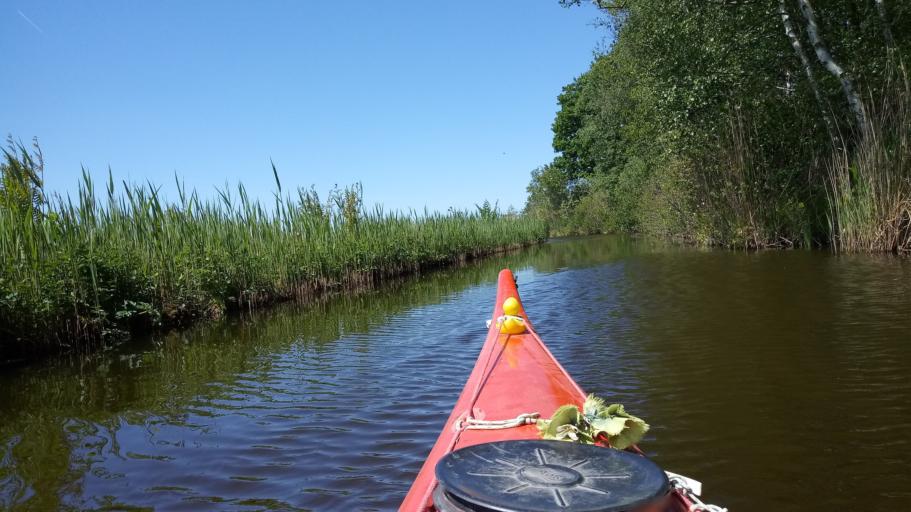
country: NL
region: South Holland
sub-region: Gemeente Nieuwkoop
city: Nieuwkoop
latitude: 52.1574
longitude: 4.8191
